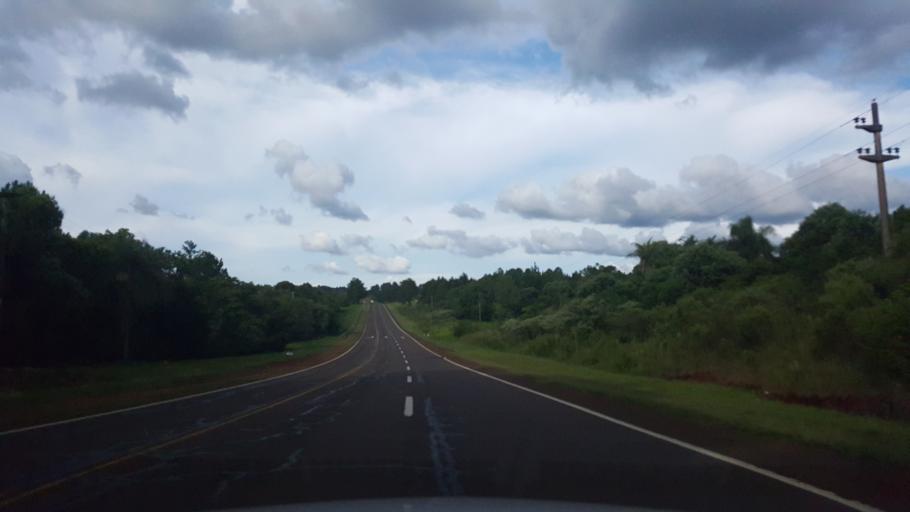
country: AR
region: Misiones
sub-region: Departamento de San Ignacio
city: San Ignacio
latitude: -27.2205
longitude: -55.5019
